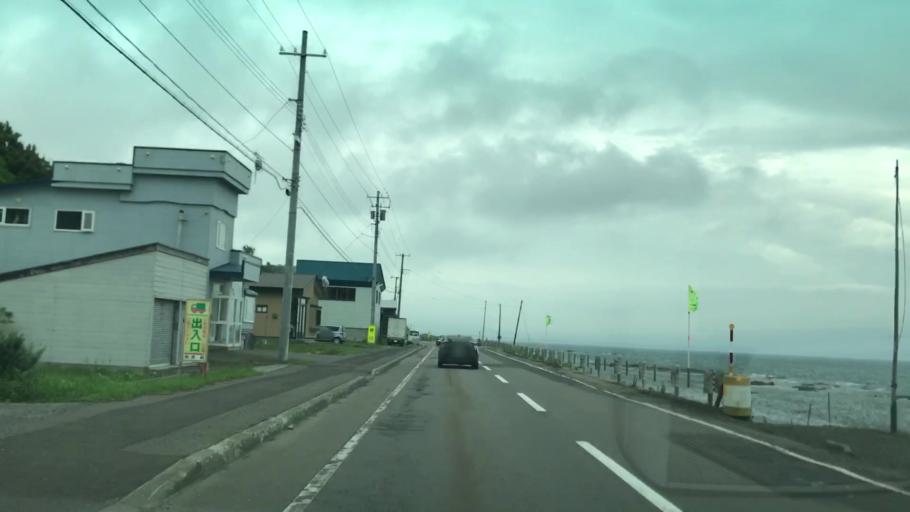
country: JP
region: Hokkaido
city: Iwanai
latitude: 42.8204
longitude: 140.3051
